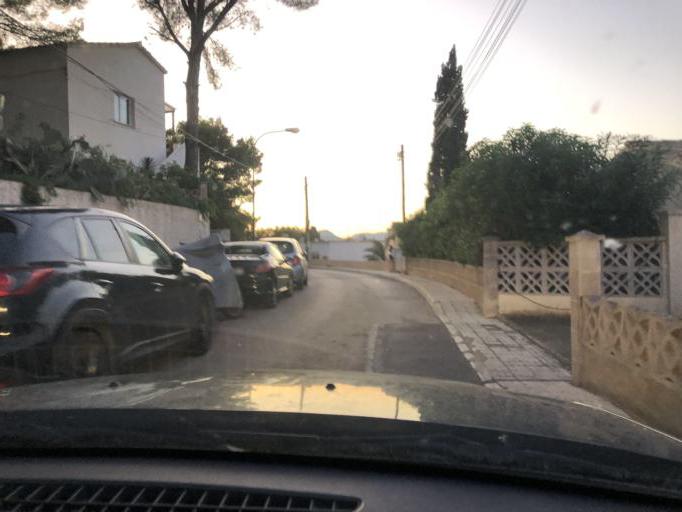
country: ES
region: Balearic Islands
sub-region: Illes Balears
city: Santa Ponsa
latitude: 39.5237
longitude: 2.4793
